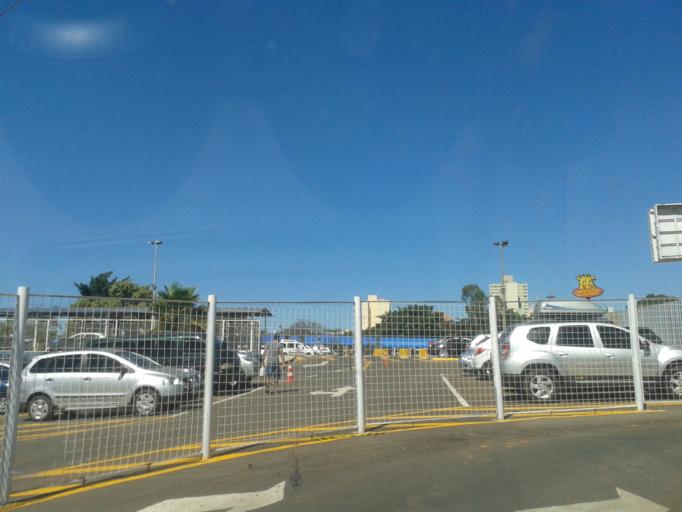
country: BR
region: Goias
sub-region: Goiania
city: Goiania
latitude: -16.6604
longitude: -49.2607
